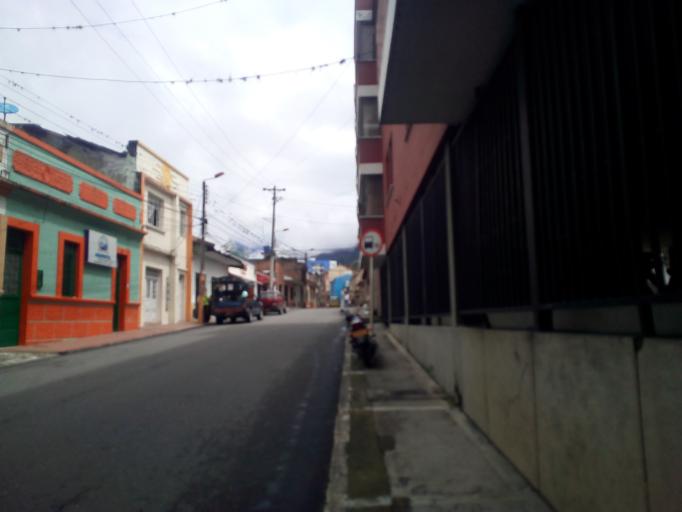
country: CO
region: Tolima
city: Ibague
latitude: 4.4439
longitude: -75.2447
